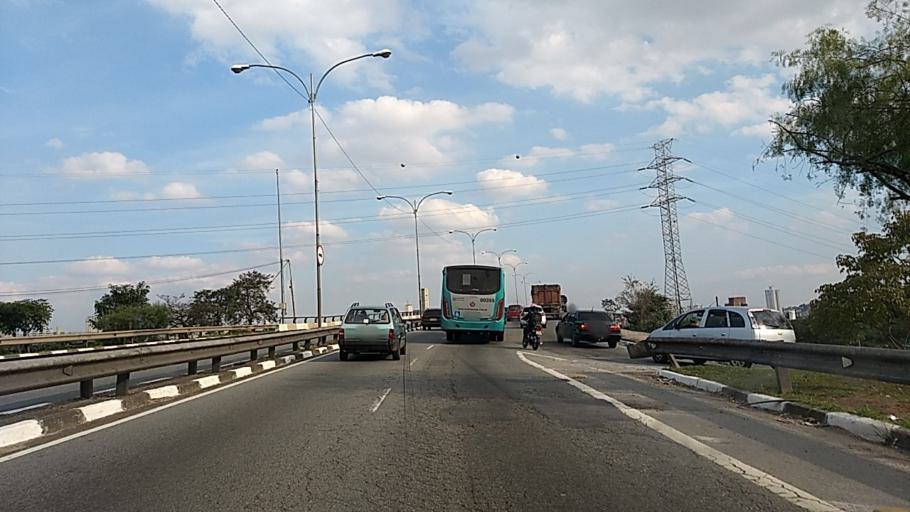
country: BR
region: Sao Paulo
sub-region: Osasco
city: Osasco
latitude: -23.5199
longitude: -46.7885
